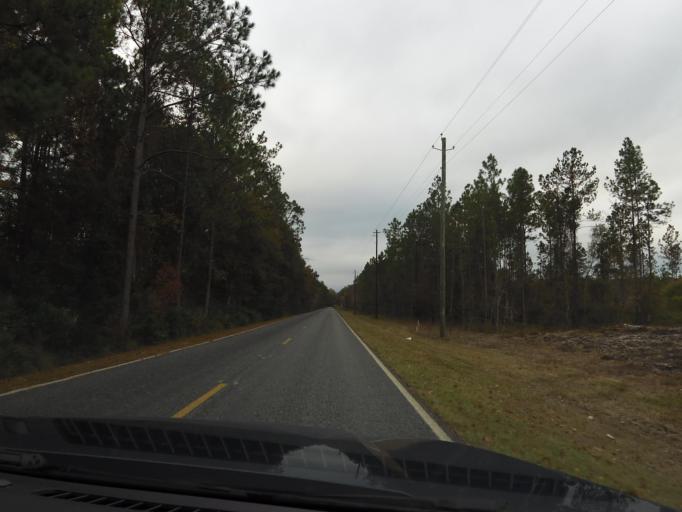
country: US
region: Georgia
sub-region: Charlton County
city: Folkston
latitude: 30.9104
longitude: -82.0798
